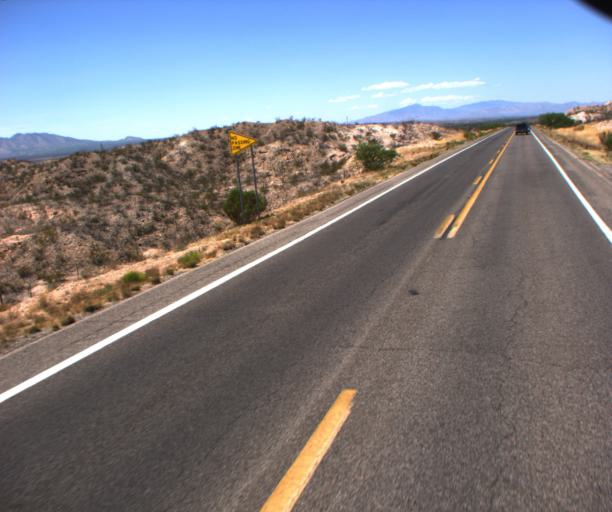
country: US
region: Arizona
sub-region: Cochise County
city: Saint David
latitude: 31.8276
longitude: -110.1784
